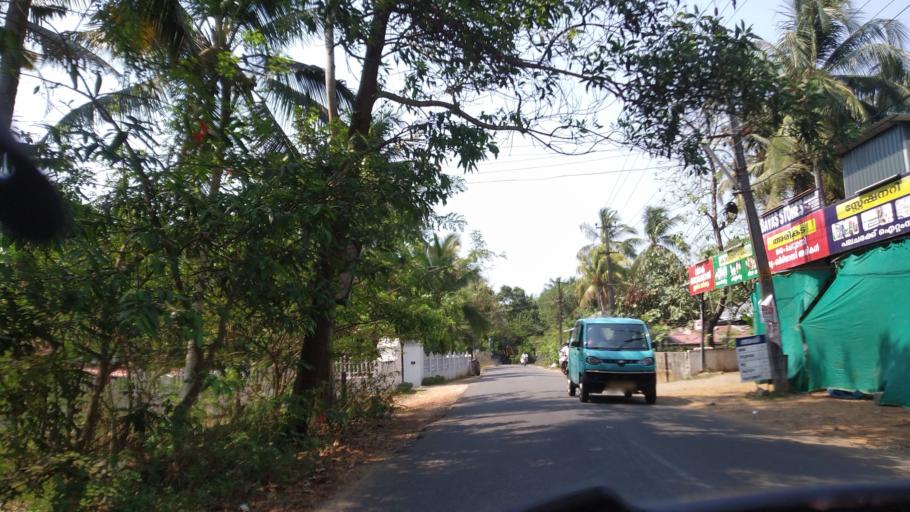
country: IN
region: Kerala
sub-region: Thrissur District
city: Kodungallur
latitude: 10.2296
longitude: 76.1548
